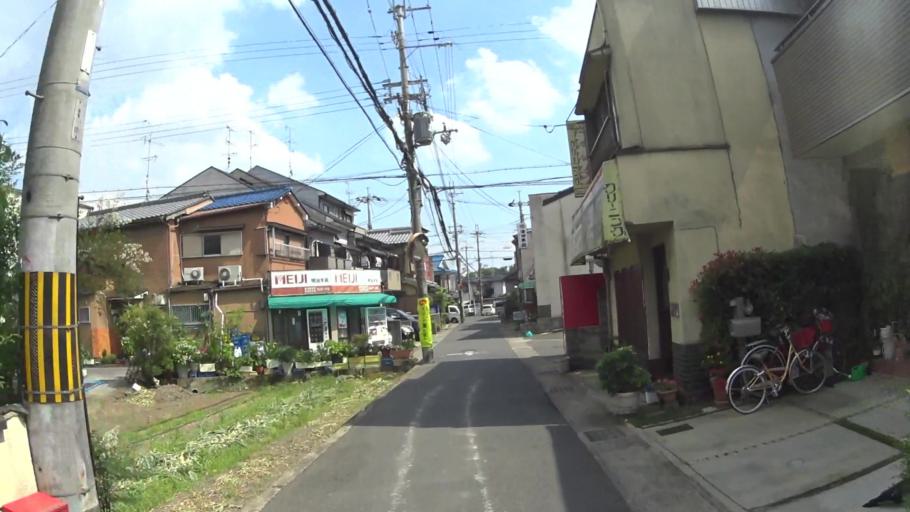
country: JP
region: Kyoto
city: Muko
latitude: 35.0074
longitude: 135.6938
